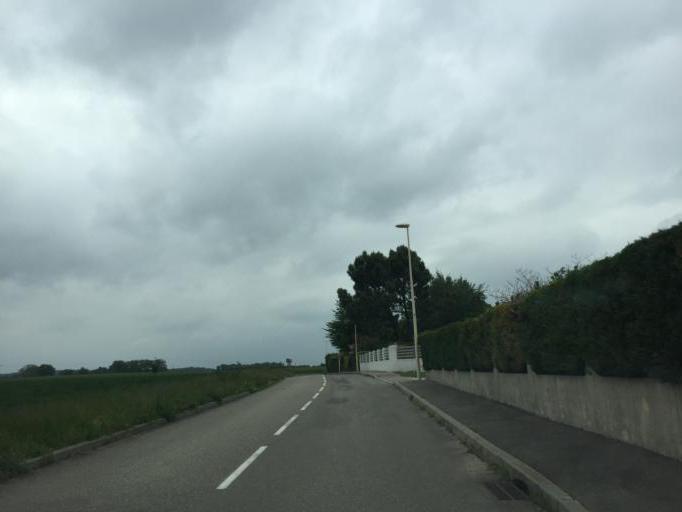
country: FR
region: Rhone-Alpes
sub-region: Departement de l'Ain
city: Miribel
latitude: 45.8236
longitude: 4.9292
